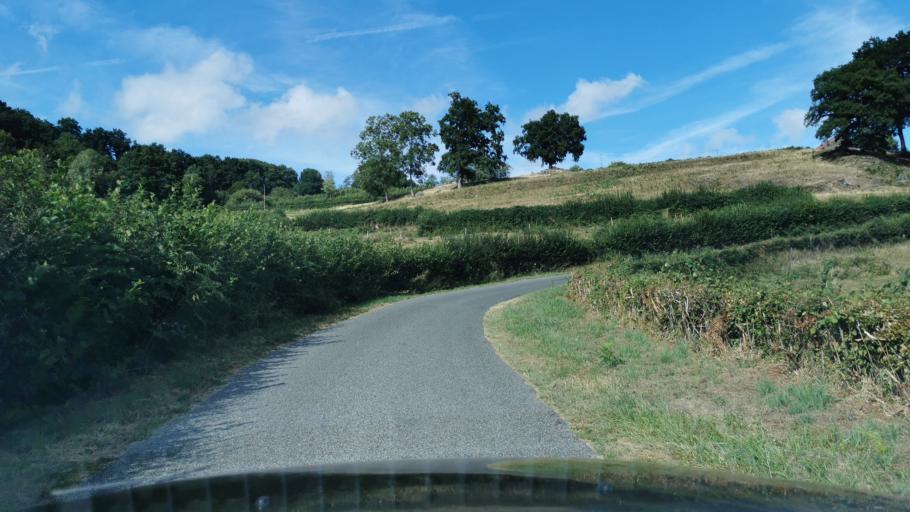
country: FR
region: Bourgogne
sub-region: Departement de Saone-et-Loire
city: Marmagne
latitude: 46.8729
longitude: 4.3345
